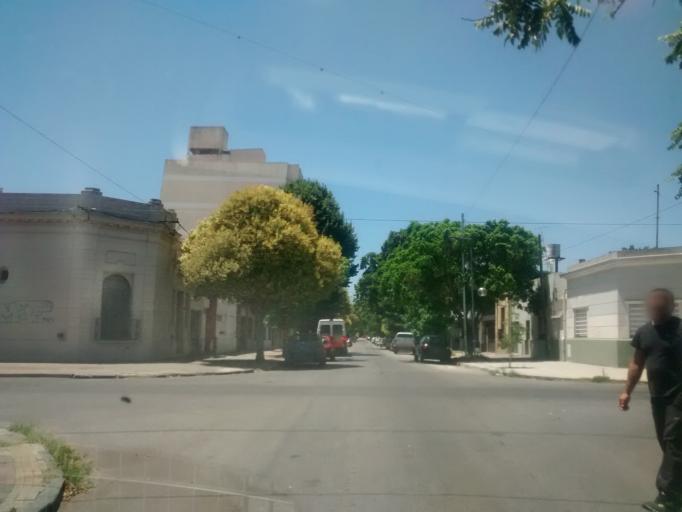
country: AR
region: Buenos Aires
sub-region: Partido de La Plata
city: La Plata
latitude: -34.9354
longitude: -57.9430
